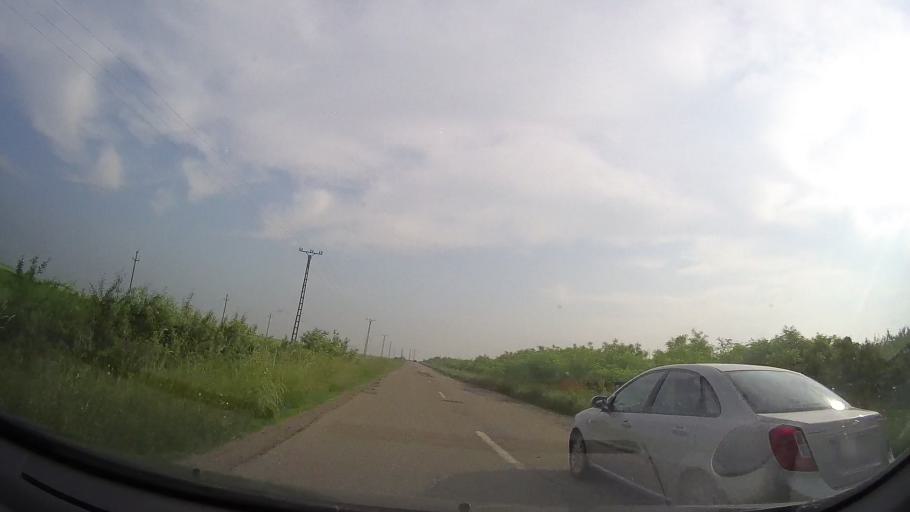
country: RO
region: Timis
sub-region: Comuna Giulvaz
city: Giulvaz
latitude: 45.5602
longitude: 20.9971
